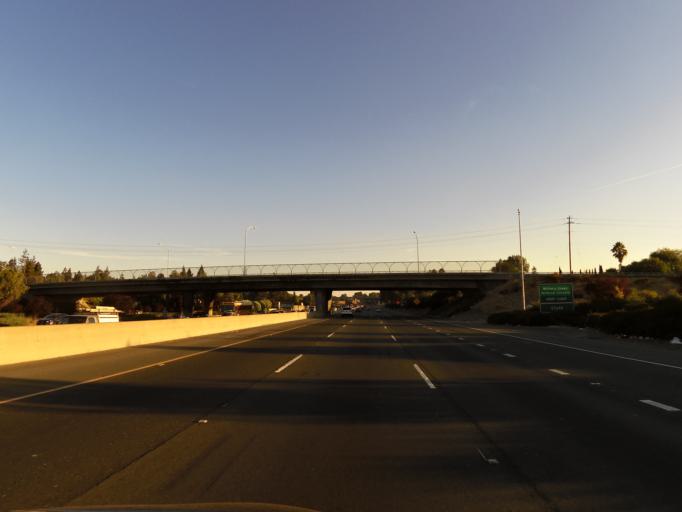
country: US
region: California
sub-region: Contra Costa County
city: Concord
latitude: 37.9965
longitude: -122.0386
